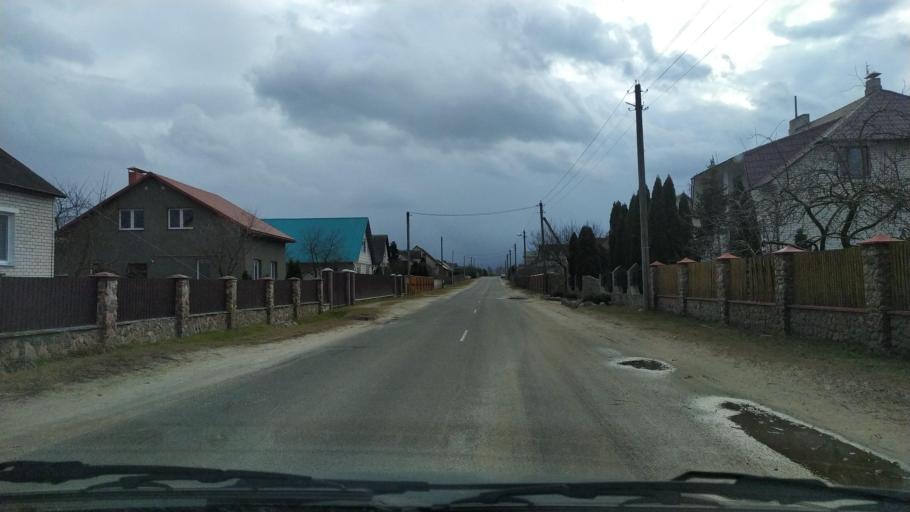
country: BY
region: Brest
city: Kamyanyets
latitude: 52.4010
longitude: 23.8418
